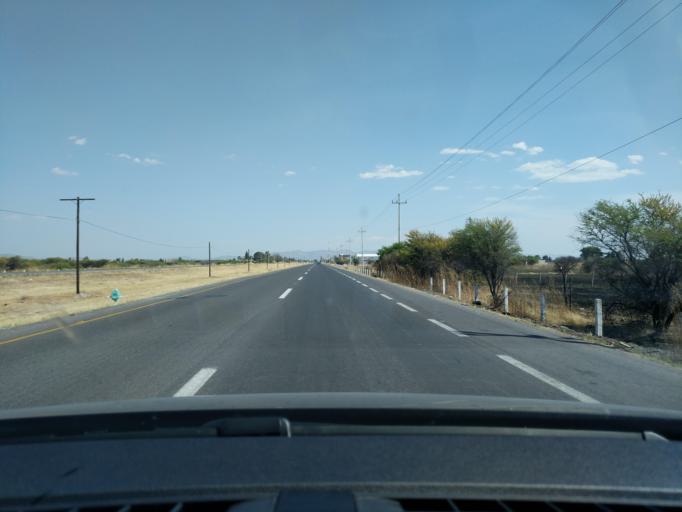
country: MX
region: Durango
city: Victoria de Durango
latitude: 24.0871
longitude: -104.5646
